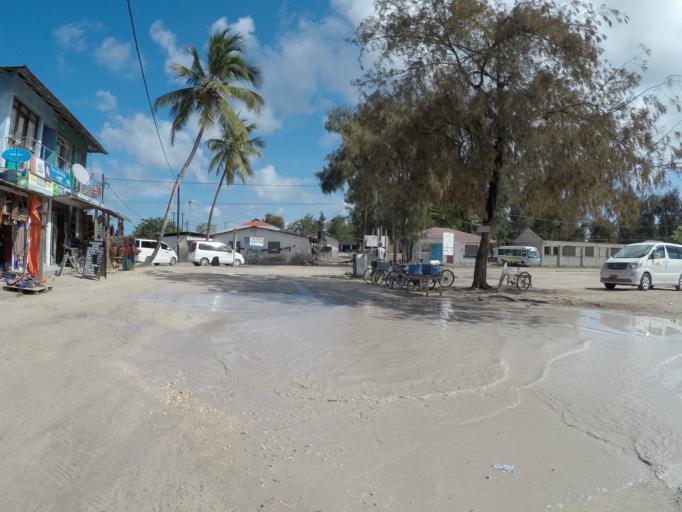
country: TZ
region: Zanzibar North
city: Nungwi
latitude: -5.7278
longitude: 39.2936
